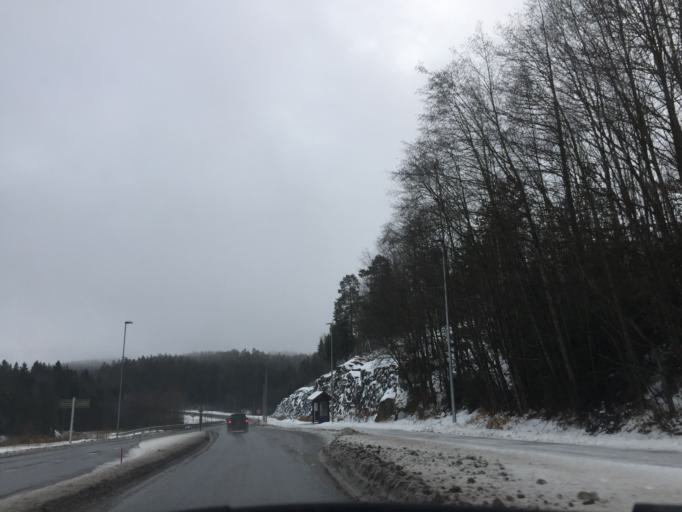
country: NO
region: Akershus
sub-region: Frogn
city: Drobak
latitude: 59.6670
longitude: 10.6596
